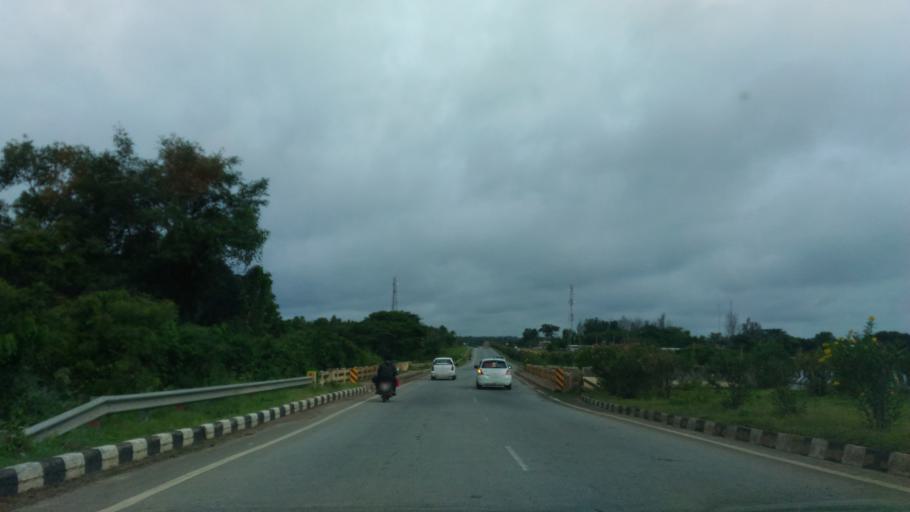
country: IN
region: Karnataka
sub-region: Bangalore Rural
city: Nelamangala
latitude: 13.0616
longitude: 77.3329
